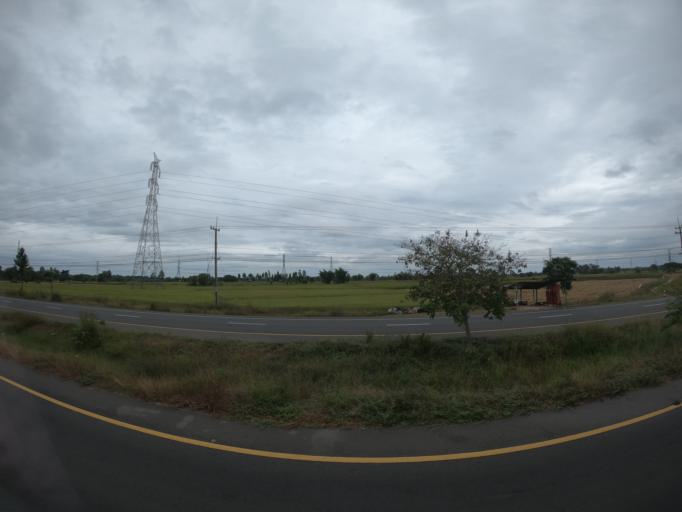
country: TH
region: Roi Et
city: Si Somdet
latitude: 16.1262
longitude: 103.4731
